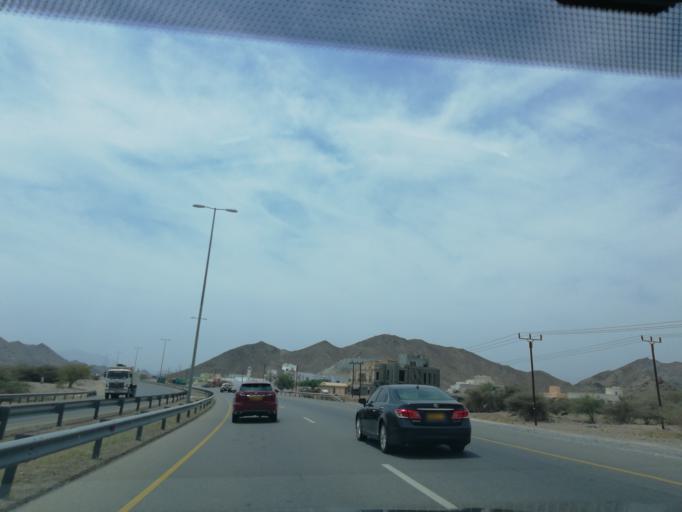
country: OM
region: Muhafazat ad Dakhiliyah
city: Bidbid
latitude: 23.4108
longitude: 58.0812
